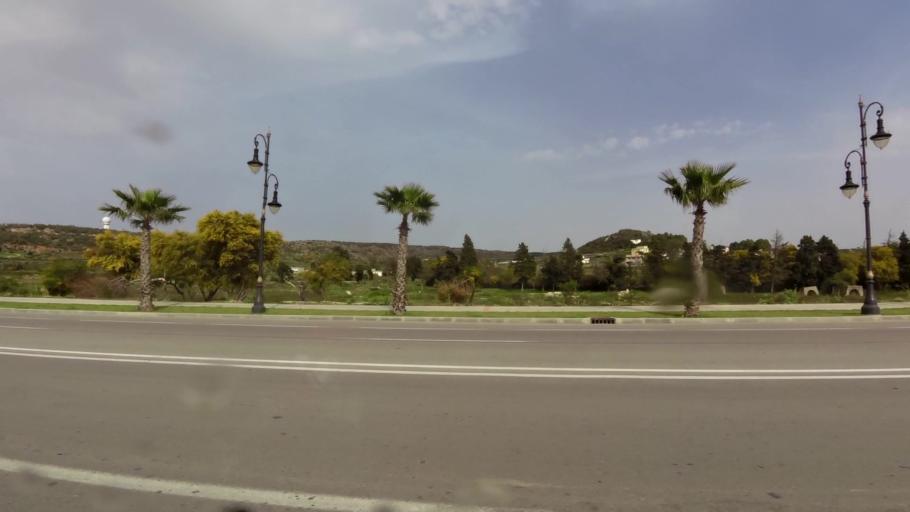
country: MA
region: Tanger-Tetouan
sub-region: Tanger-Assilah
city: Boukhalef
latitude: 35.6921
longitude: -5.9166
